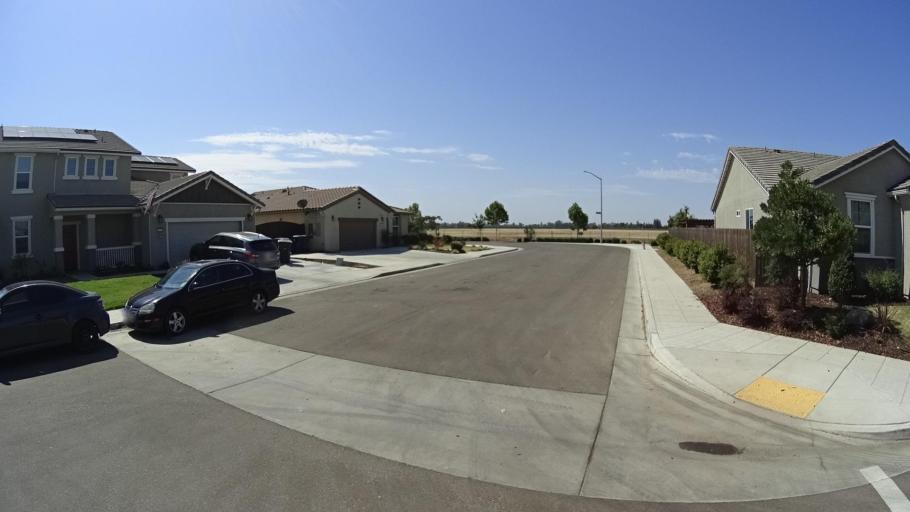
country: US
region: California
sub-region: Fresno County
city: Sunnyside
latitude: 36.7709
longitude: -119.6556
